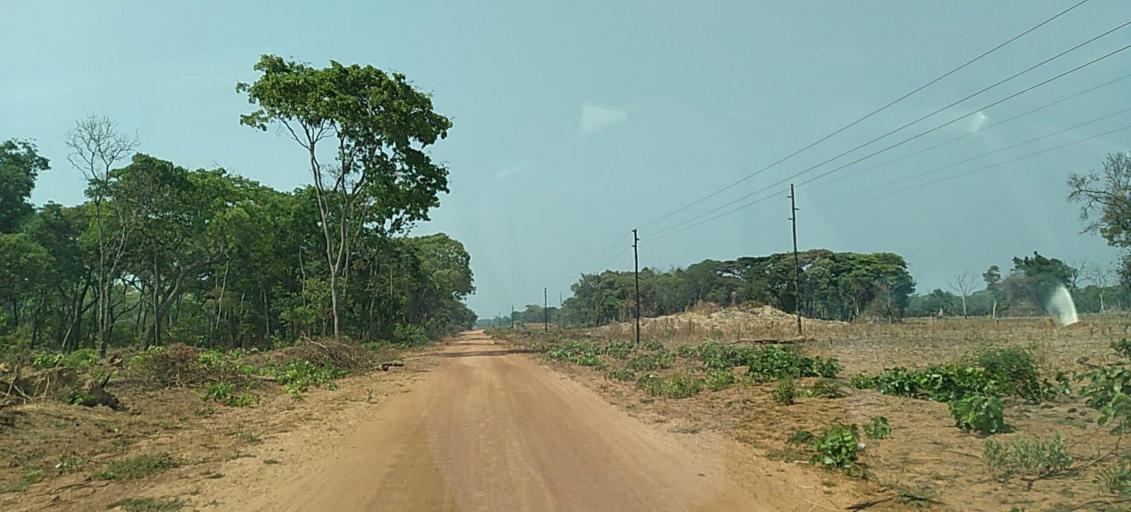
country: ZM
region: Copperbelt
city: Kalulushi
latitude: -13.0925
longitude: 27.4071
